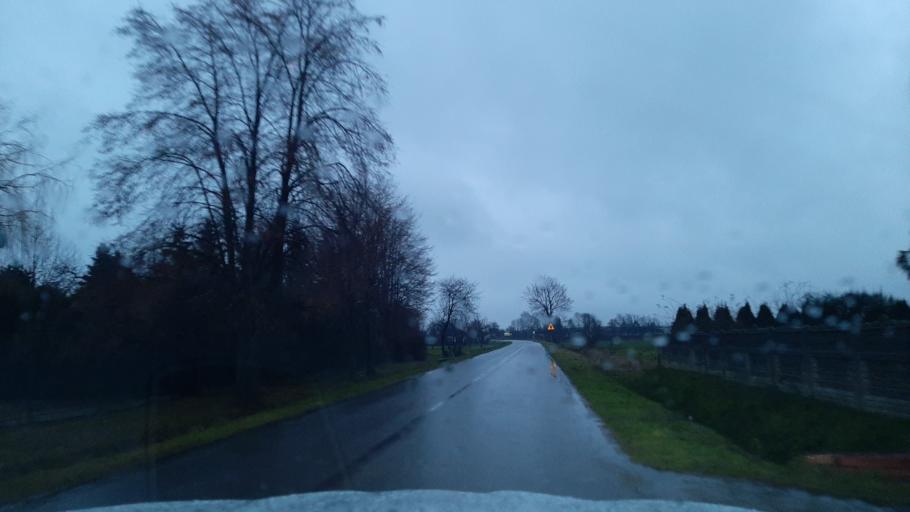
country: PL
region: Lublin Voivodeship
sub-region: Powiat lubelski
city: Jastkow
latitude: 51.3533
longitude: 22.4031
